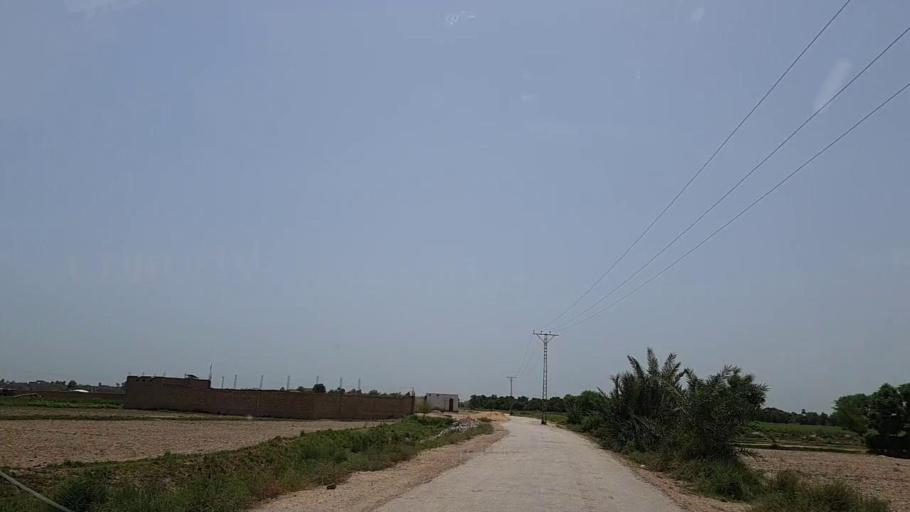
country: PK
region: Sindh
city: Tharu Shah
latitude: 26.9460
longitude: 68.1069
